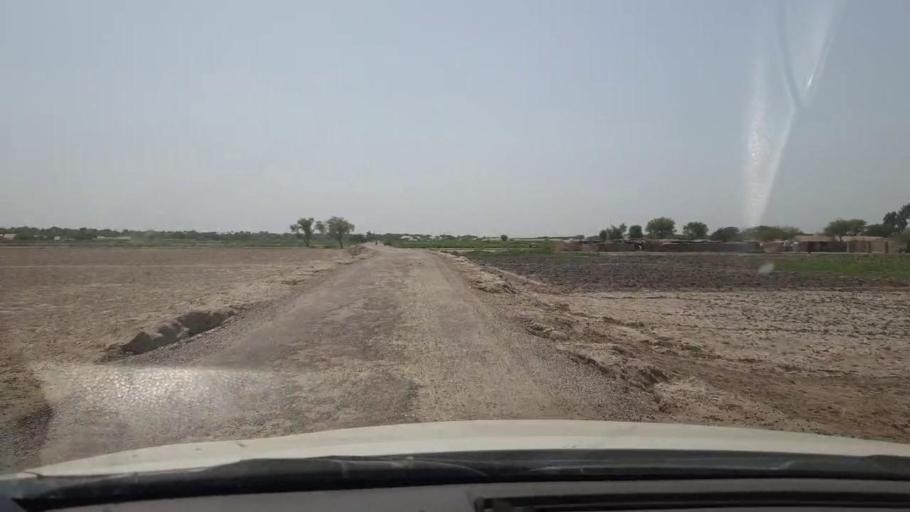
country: PK
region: Sindh
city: Rohri
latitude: 27.5183
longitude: 69.0839
